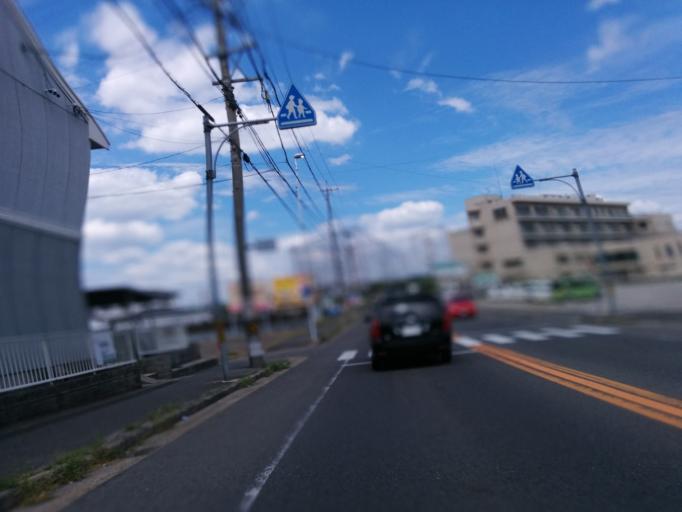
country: JP
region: Aichi
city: Kasugai
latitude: 35.2714
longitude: 136.9855
